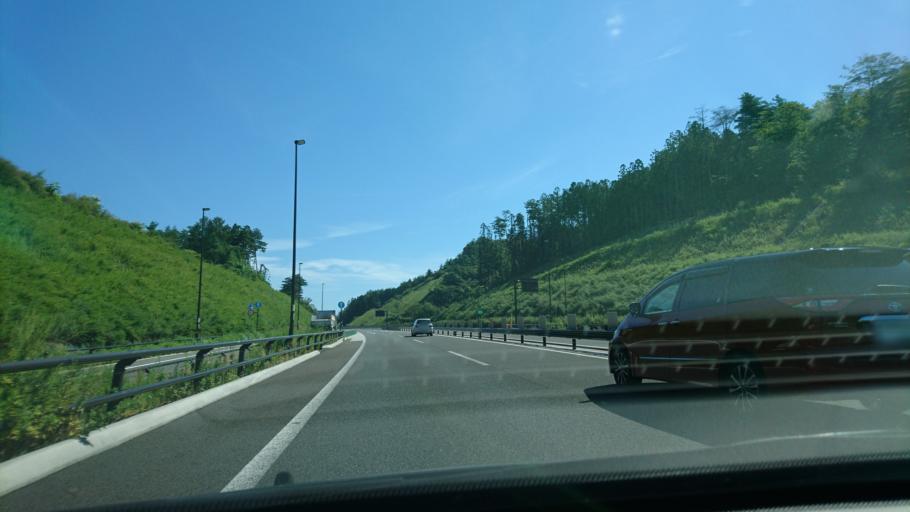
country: JP
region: Iwate
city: Tono
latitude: 39.2947
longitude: 141.4065
